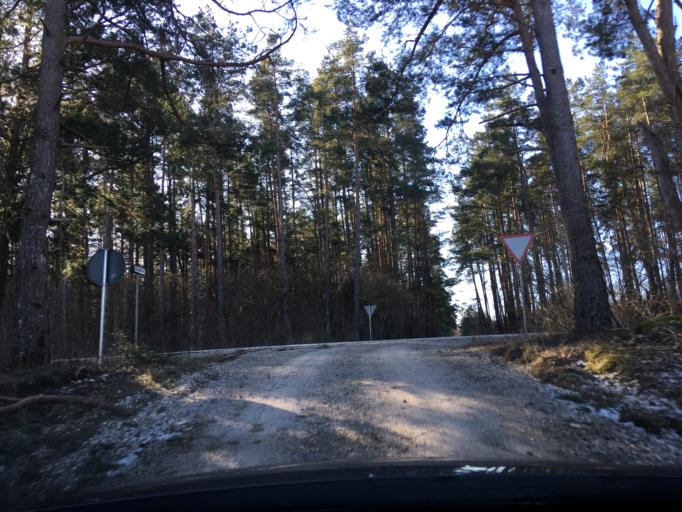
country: EE
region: Laeaene
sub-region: Lihula vald
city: Lihula
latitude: 58.5676
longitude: 23.6918
